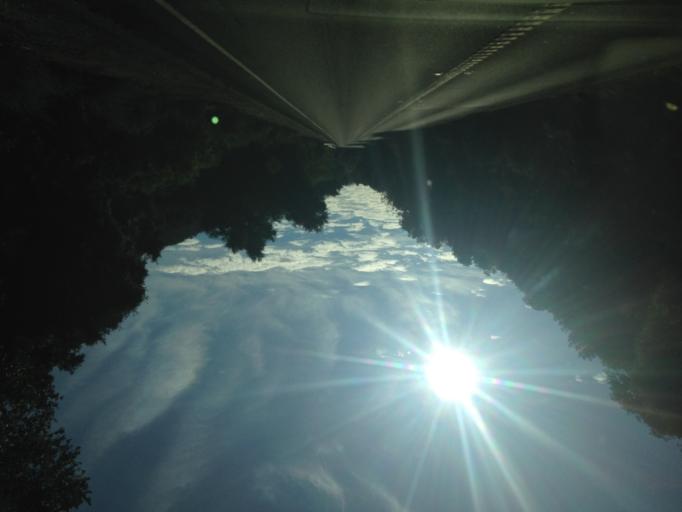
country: US
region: California
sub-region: Riverside County
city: Aguanga
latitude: 33.2446
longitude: -116.7807
